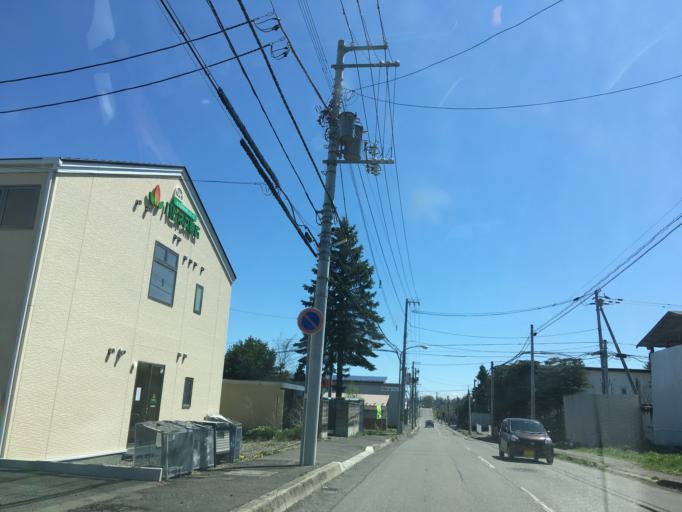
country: JP
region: Hokkaido
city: Obihiro
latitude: 42.9292
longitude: 143.1771
